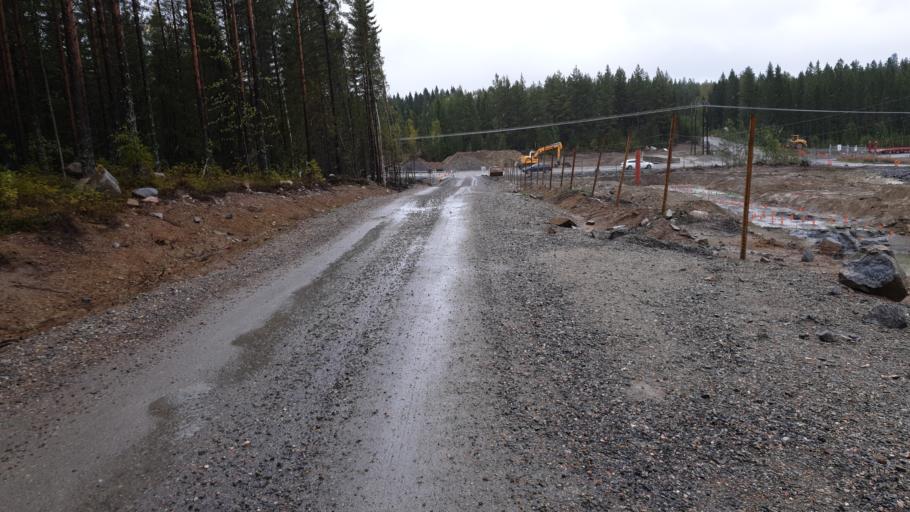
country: SE
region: Vaesterbotten
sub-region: Skelleftea Kommun
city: Soedra Bergsbyn
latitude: 64.7398
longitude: 21.0751
